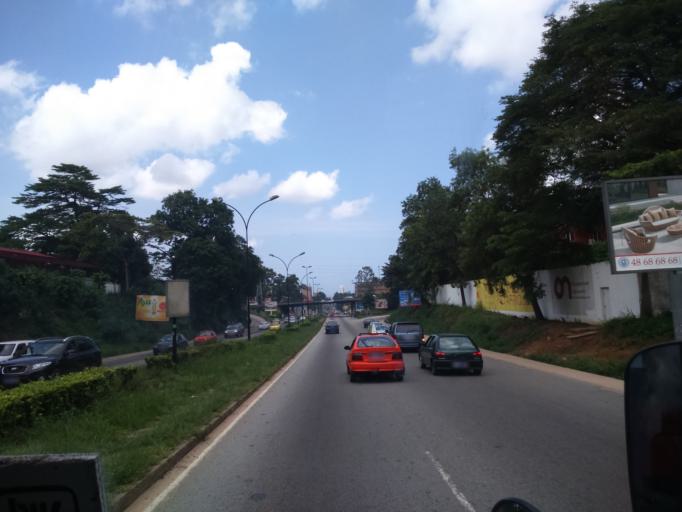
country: CI
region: Lagunes
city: Abidjan
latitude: 5.3565
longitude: -4.0015
